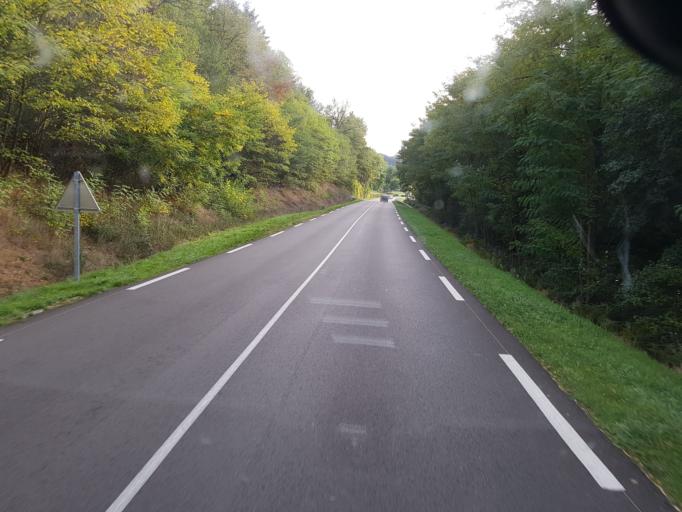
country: FR
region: Bourgogne
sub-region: Departement de Saone-et-Loire
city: La Clayette
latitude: 46.2838
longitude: 4.3513
